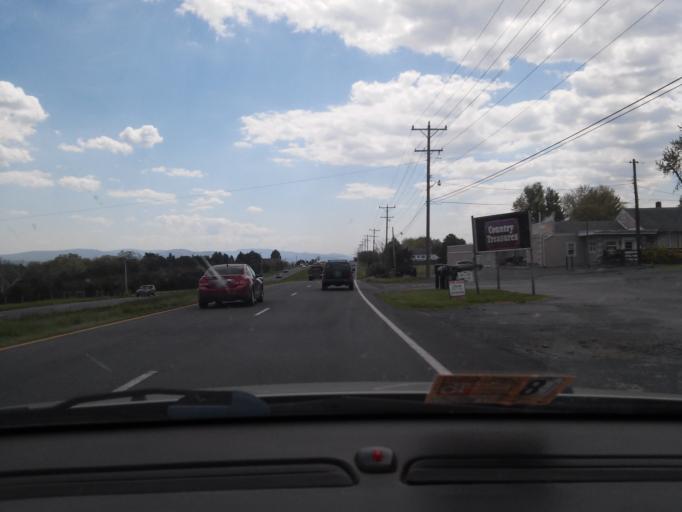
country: US
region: Virginia
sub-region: Frederick County
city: Stephens City
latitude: 39.0337
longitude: -78.1533
